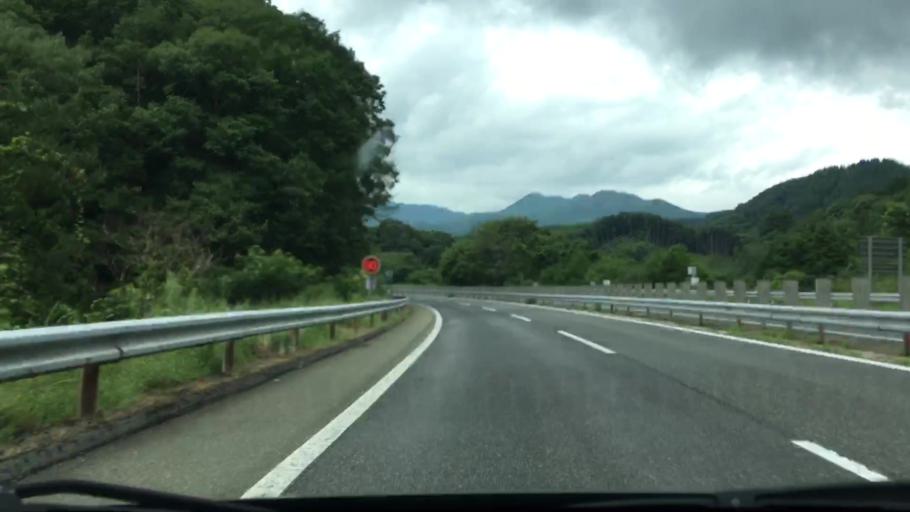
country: JP
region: Okayama
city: Niimi
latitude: 34.8918
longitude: 133.2616
